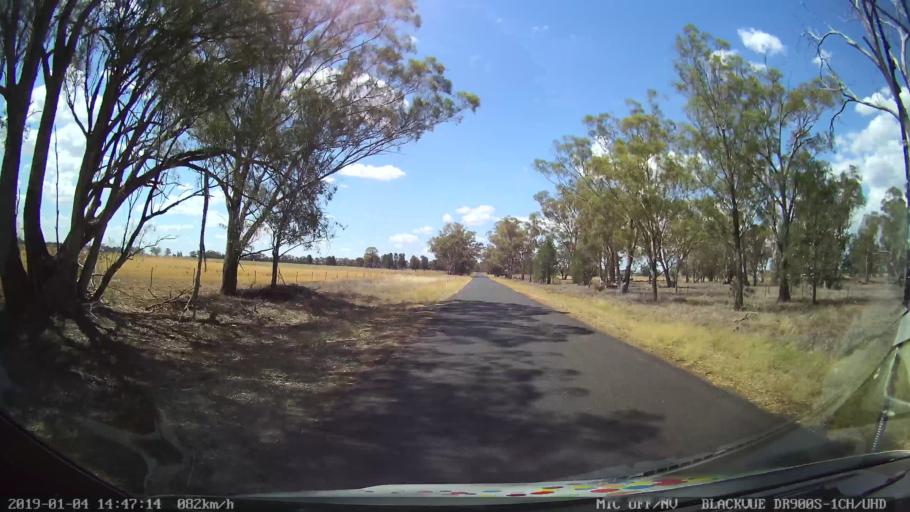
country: AU
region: New South Wales
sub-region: Dubbo Municipality
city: Dubbo
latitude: -32.0716
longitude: 148.6598
